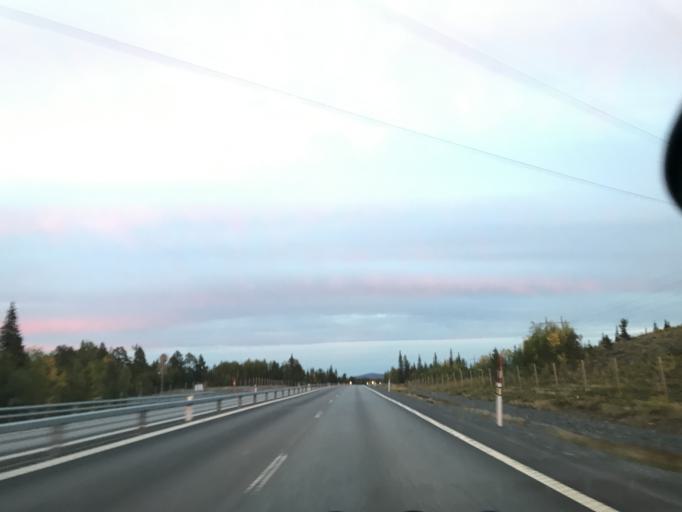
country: SE
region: Norrbotten
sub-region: Gallivare Kommun
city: Malmberget
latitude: 67.6926
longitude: 20.8219
